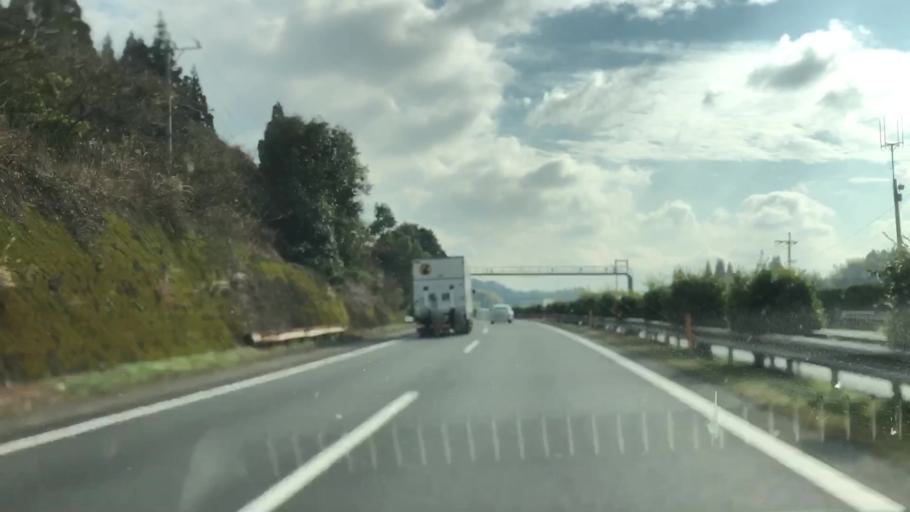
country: JP
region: Fukuoka
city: Setakamachi-takayanagi
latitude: 33.0889
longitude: 130.5395
